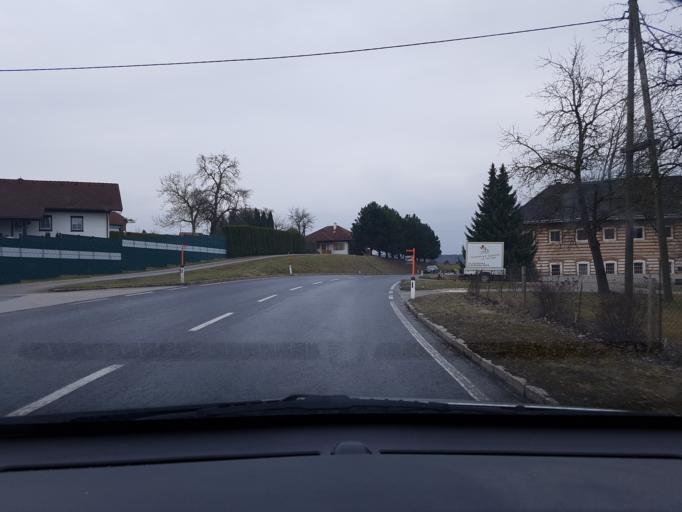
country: AT
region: Upper Austria
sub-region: Steyr Stadt
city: Steyr
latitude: 48.0762
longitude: 14.3818
